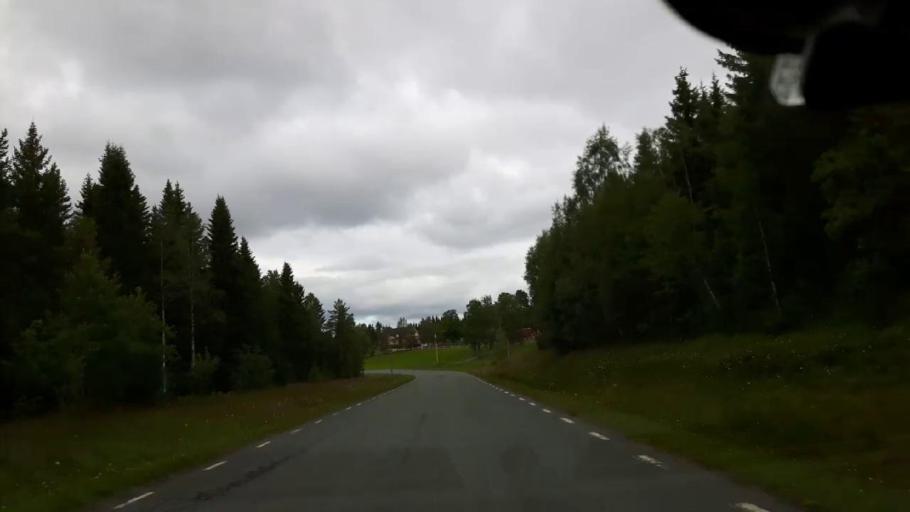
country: SE
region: Jaemtland
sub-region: Krokoms Kommun
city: Valla
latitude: 63.5342
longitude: 13.8716
